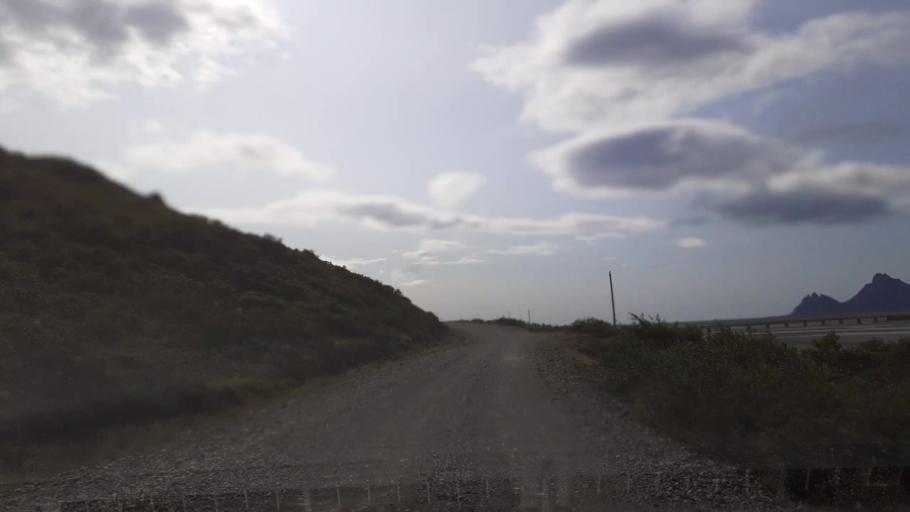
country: IS
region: East
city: Hoefn
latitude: 64.4265
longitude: -14.8833
